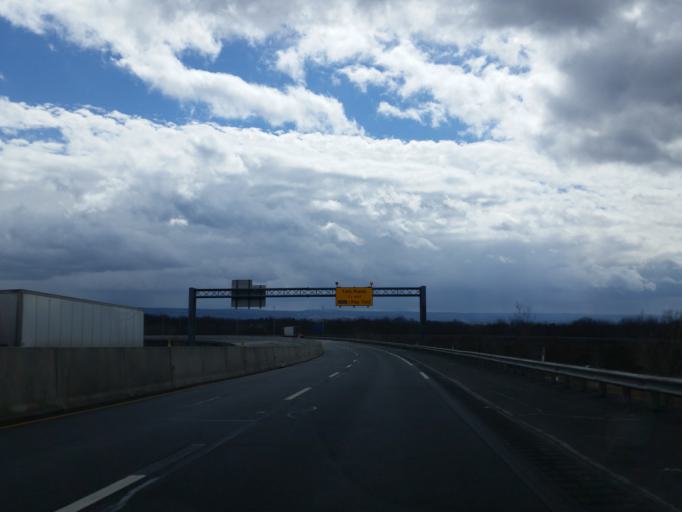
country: US
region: Pennsylvania
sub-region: Lackawanna County
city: Old Forge
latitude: 41.3906
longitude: -75.7326
